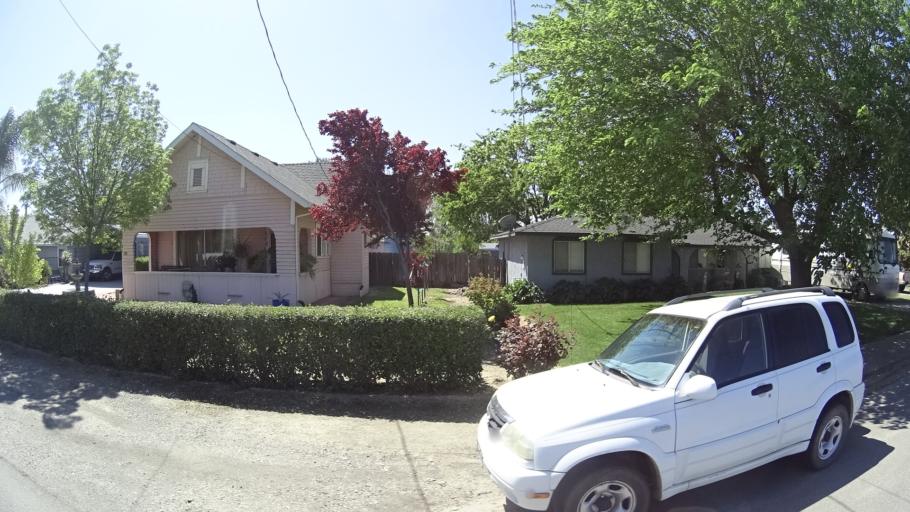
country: US
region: California
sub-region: Glenn County
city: Orland
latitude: 39.7474
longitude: -122.2015
